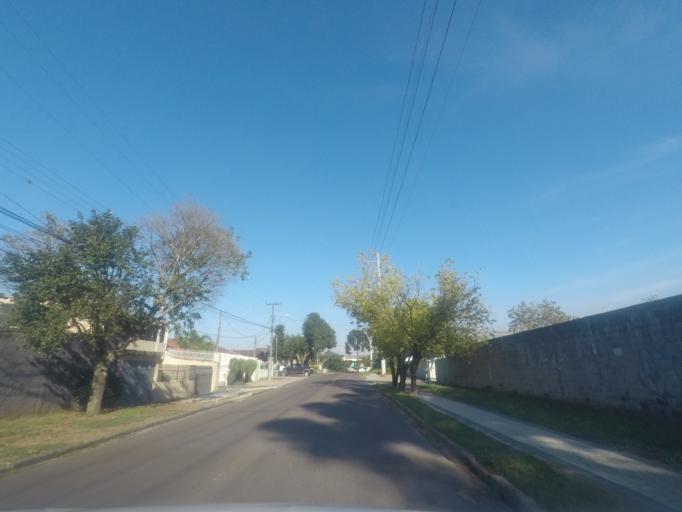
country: BR
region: Parana
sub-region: Pinhais
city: Pinhais
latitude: -25.4719
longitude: -49.2157
